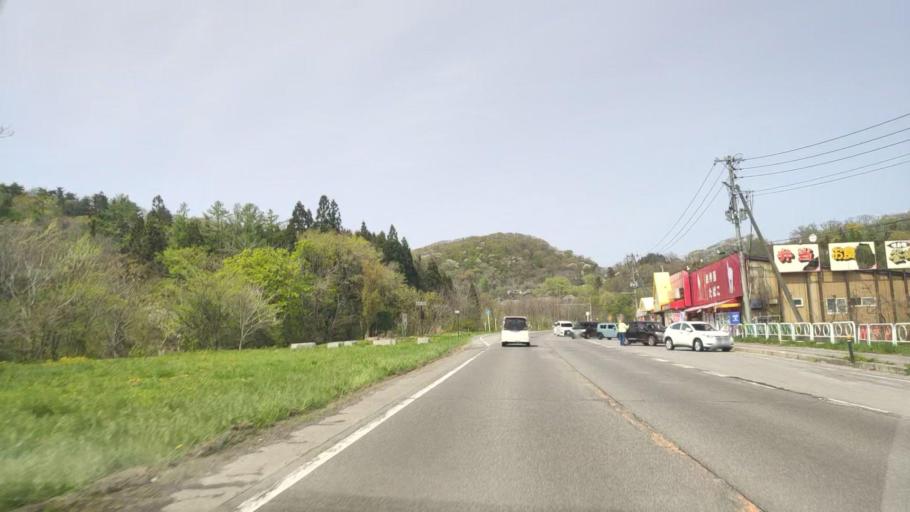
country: JP
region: Aomori
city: Aomori Shi
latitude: 40.8521
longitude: 140.8383
